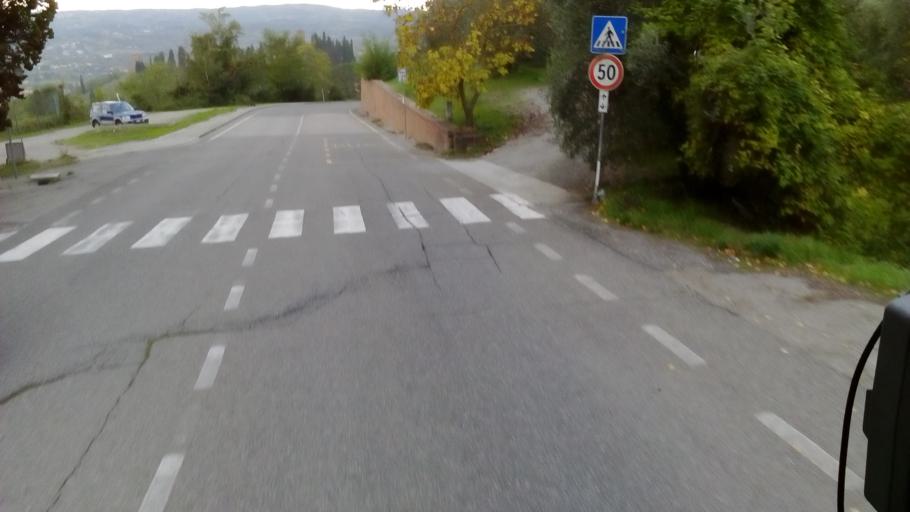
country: IT
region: Tuscany
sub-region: Province of Florence
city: Castelfiorentino
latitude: 43.6117
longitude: 10.9758
